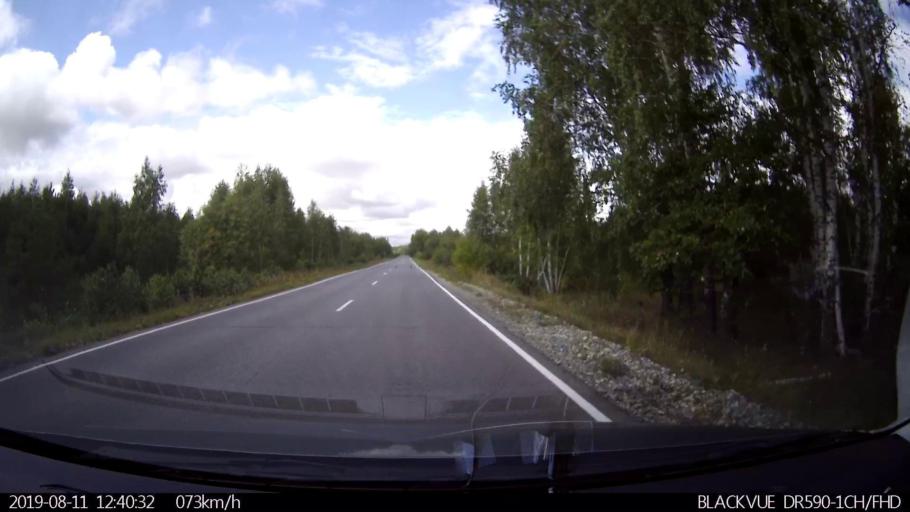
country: RU
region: Ulyanovsk
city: Ignatovka
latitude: 53.8392
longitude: 47.7794
